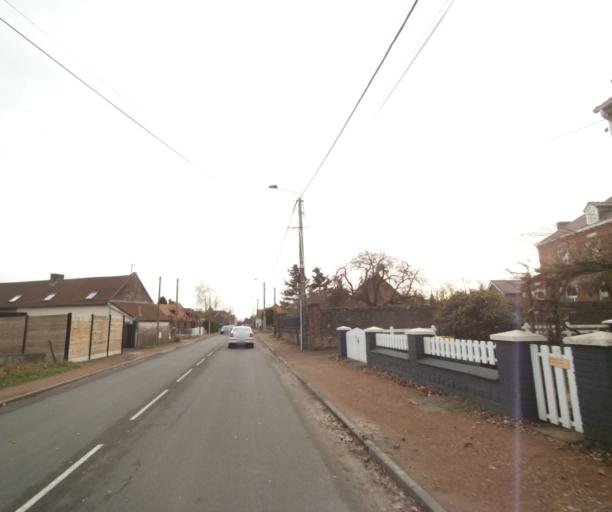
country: FR
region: Nord-Pas-de-Calais
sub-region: Departement du Nord
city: Hergnies
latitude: 50.4692
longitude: 3.5387
